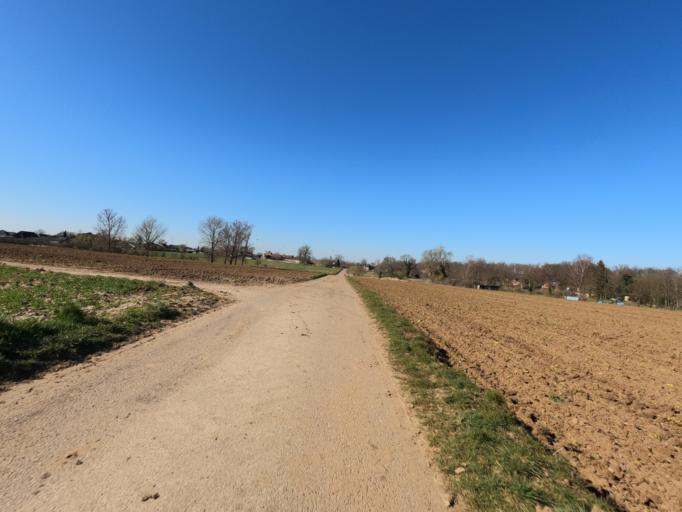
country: DE
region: North Rhine-Westphalia
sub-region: Regierungsbezirk Koln
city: Linnich
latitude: 50.9563
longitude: 6.2645
